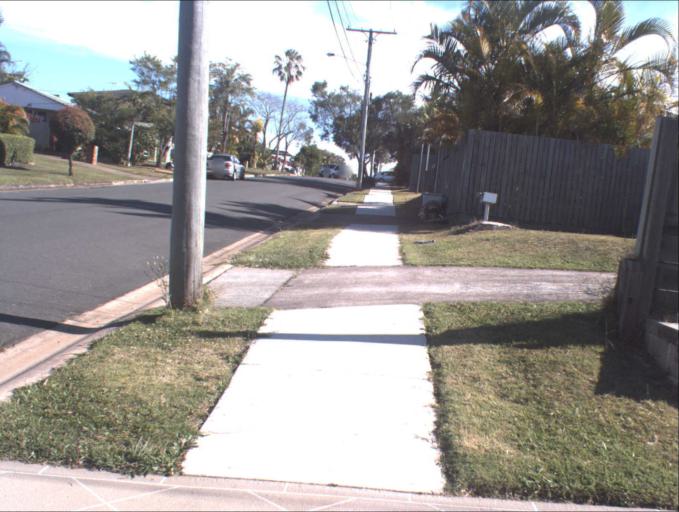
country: AU
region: Queensland
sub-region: Logan
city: Slacks Creek
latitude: -27.6483
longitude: 153.1336
